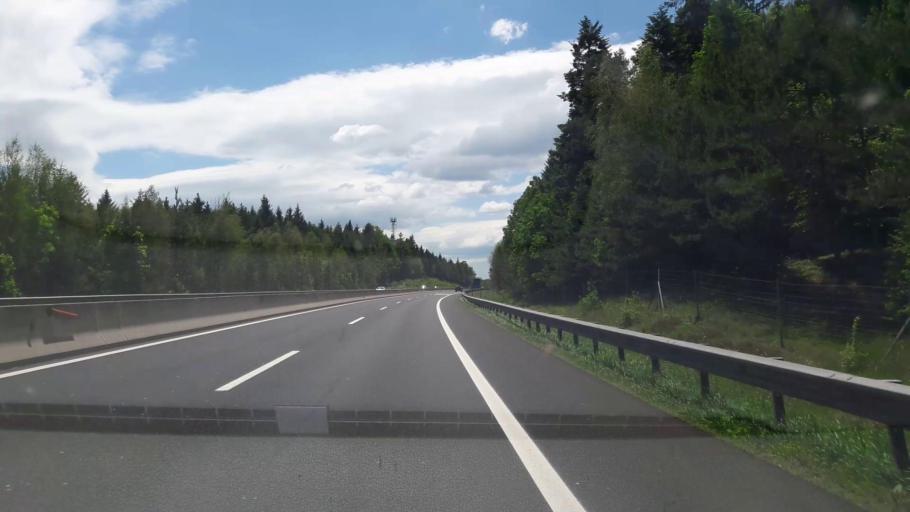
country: AT
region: Styria
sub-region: Politischer Bezirk Hartberg-Fuerstenfeld
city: Pinggau
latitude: 47.4039
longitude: 16.0812
